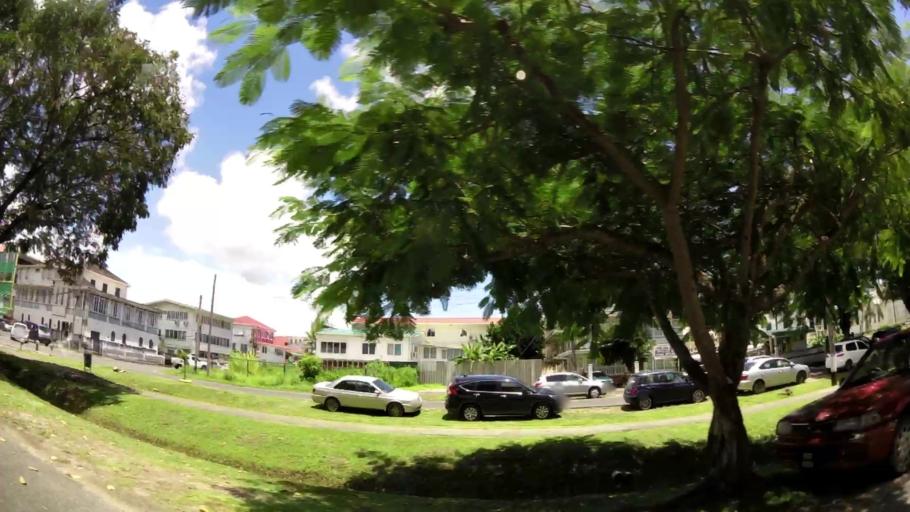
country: GY
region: Demerara-Mahaica
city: Georgetown
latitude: 6.8166
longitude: -58.1625
